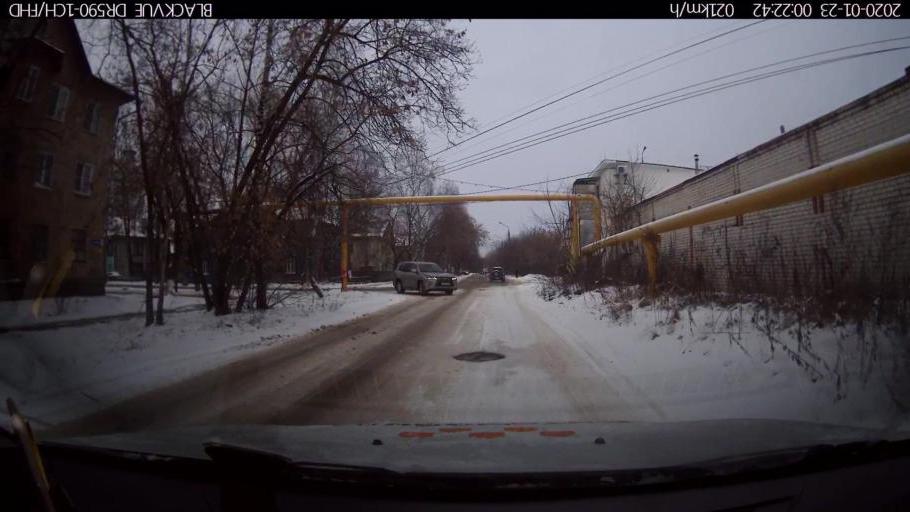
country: RU
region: Nizjnij Novgorod
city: Gorbatovka
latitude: 56.3652
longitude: 43.8303
